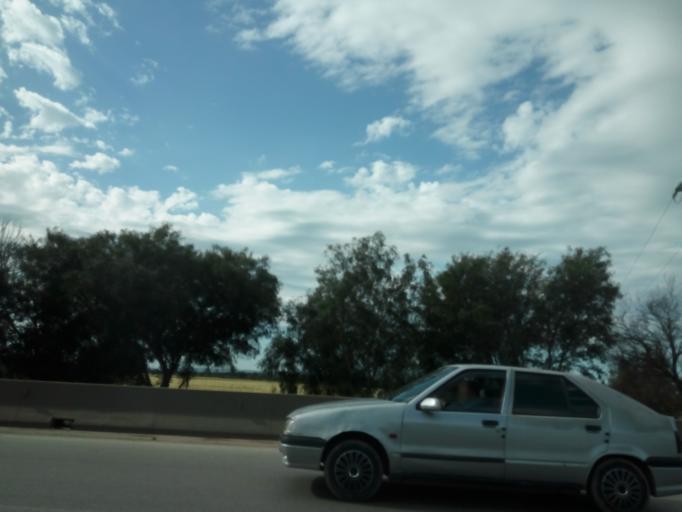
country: DZ
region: Blida
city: Chiffa
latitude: 36.4509
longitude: 2.7272
